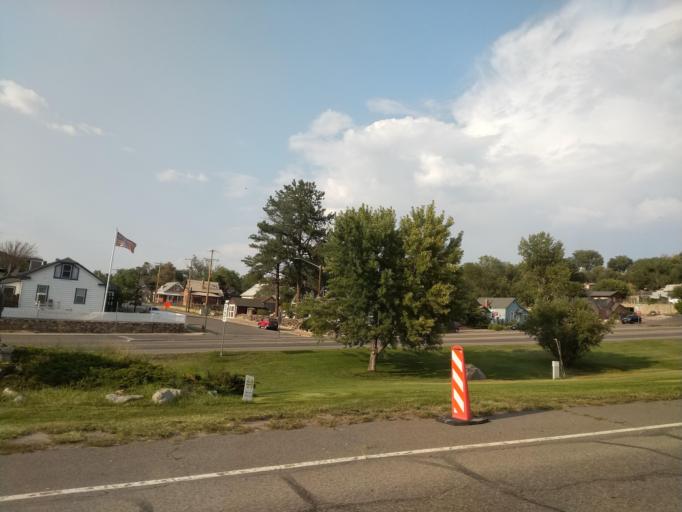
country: US
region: Colorado
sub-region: Garfield County
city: Rifle
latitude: 39.5293
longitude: -107.7823
